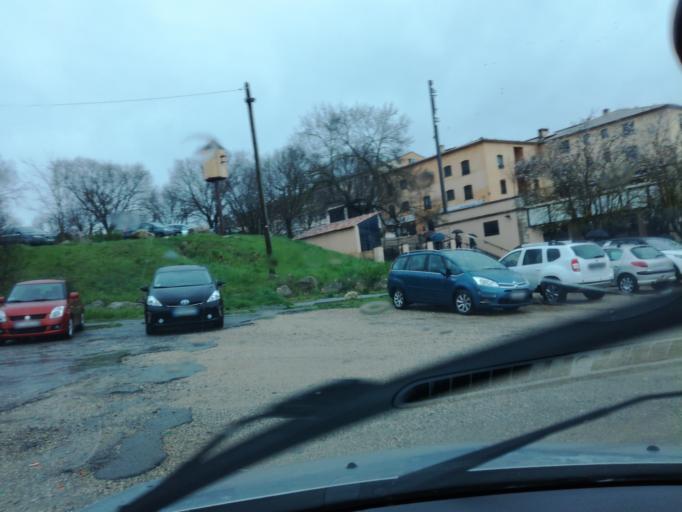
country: FR
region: Provence-Alpes-Cote d'Azur
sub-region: Departement des Alpes-Maritimes
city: Valbonne
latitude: 43.6418
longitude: 7.0058
